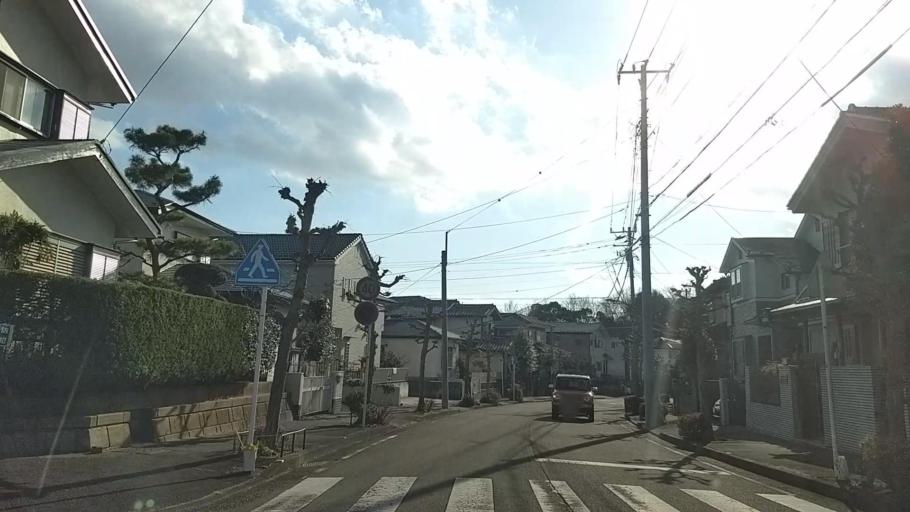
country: JP
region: Kanagawa
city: Atsugi
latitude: 35.4371
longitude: 139.3286
